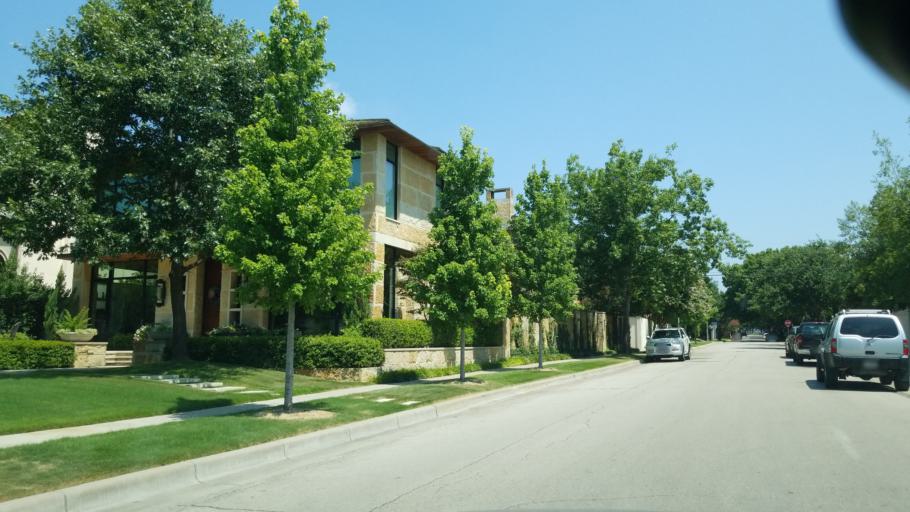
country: US
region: Texas
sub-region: Dallas County
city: Highland Park
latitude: 32.8324
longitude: -96.7834
